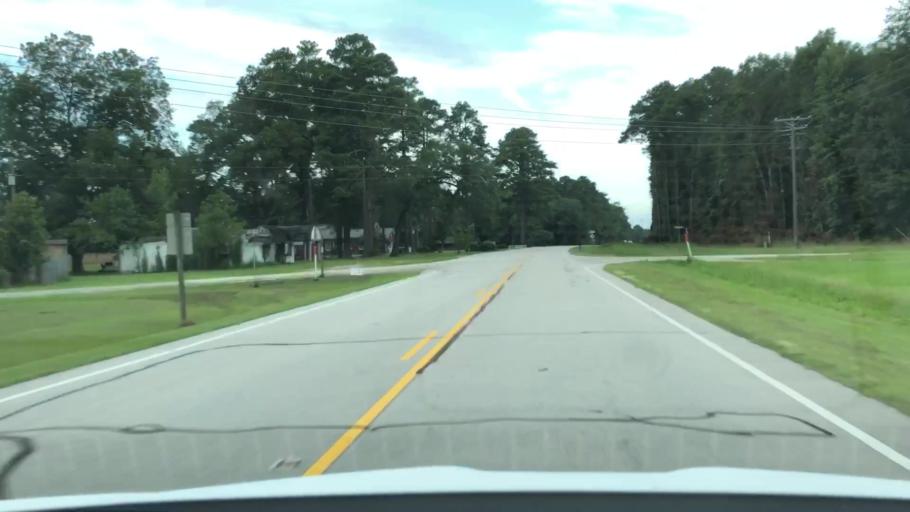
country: US
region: North Carolina
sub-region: Lenoir County
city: Kinston
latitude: 35.1201
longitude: -77.5161
